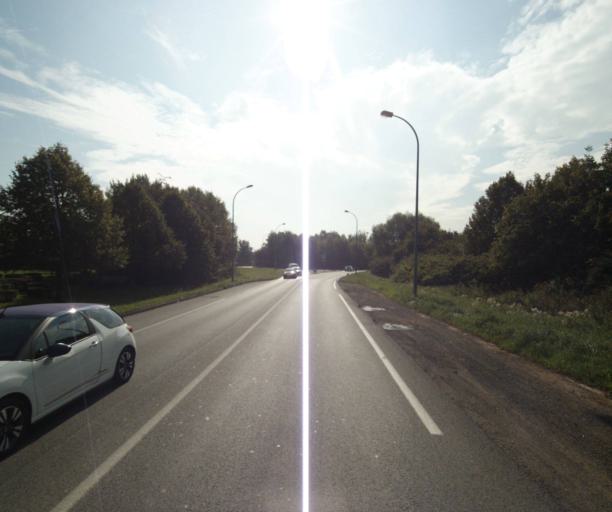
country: FR
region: Nord-Pas-de-Calais
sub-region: Departement du Nord
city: Seclin
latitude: 50.5493
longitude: 3.0477
